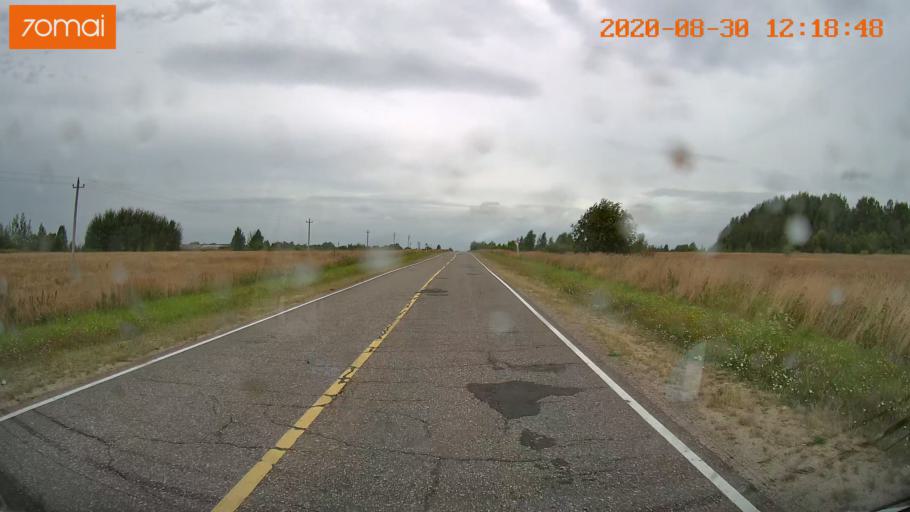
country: RU
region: Ivanovo
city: Yur'yevets
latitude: 57.3232
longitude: 42.9430
